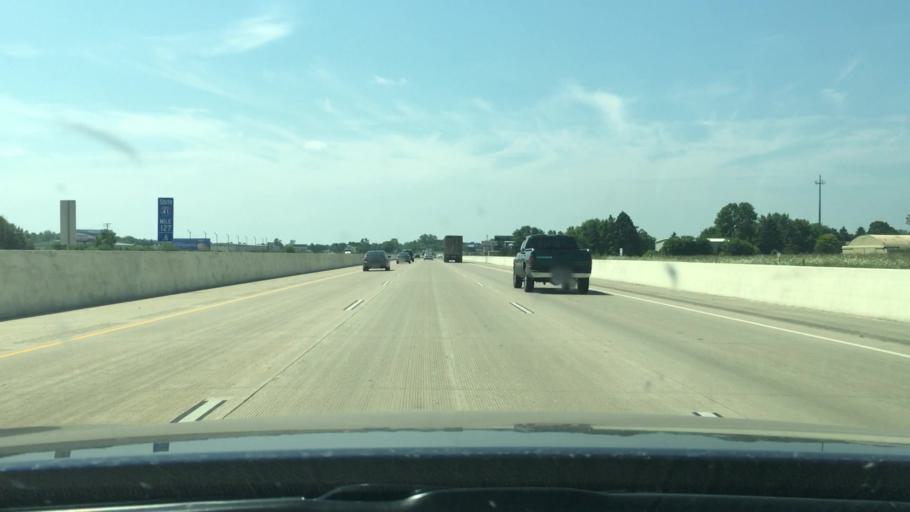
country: US
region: Wisconsin
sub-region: Winnebago County
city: Neenah
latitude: 44.1340
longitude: -88.4950
